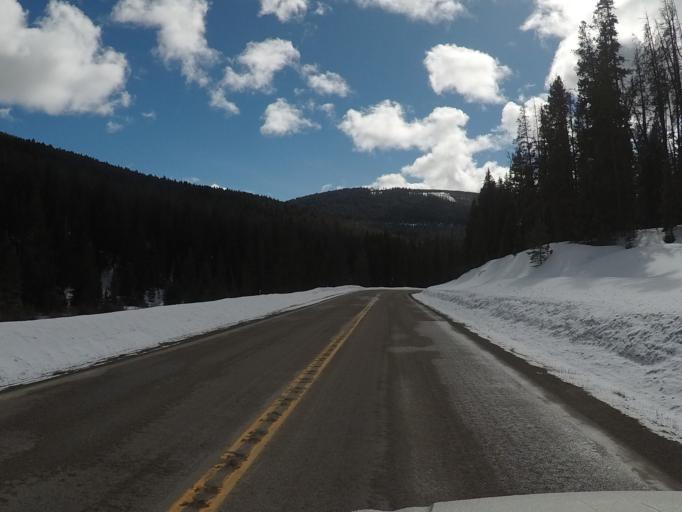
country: US
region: Montana
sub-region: Meagher County
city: White Sulphur Springs
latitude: 46.7648
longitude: -110.7129
